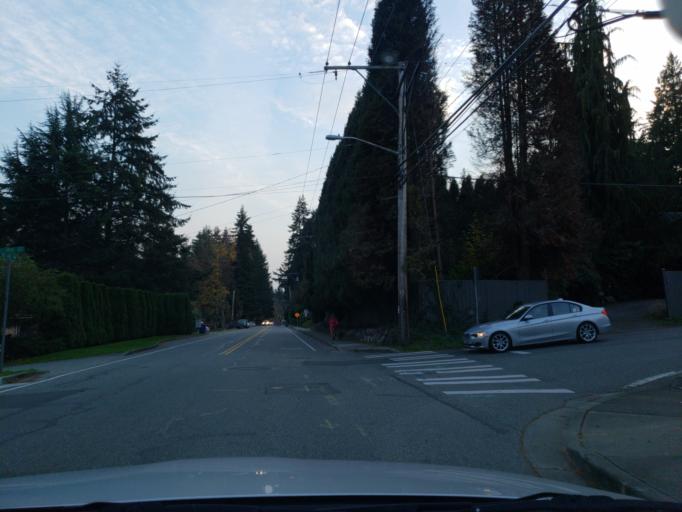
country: US
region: Washington
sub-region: King County
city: Bothell
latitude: 47.7659
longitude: -122.2177
